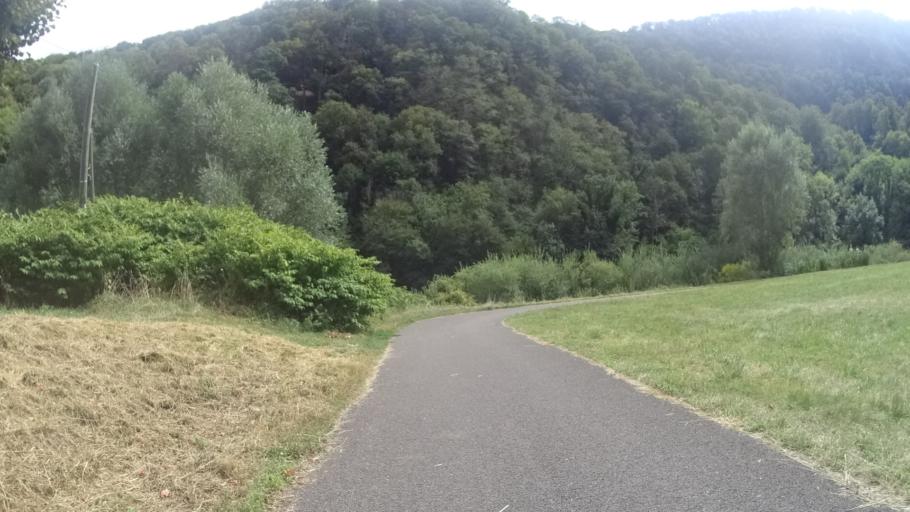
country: FR
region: Franche-Comte
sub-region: Departement du Doubs
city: Roulans
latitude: 47.2966
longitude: 6.2334
